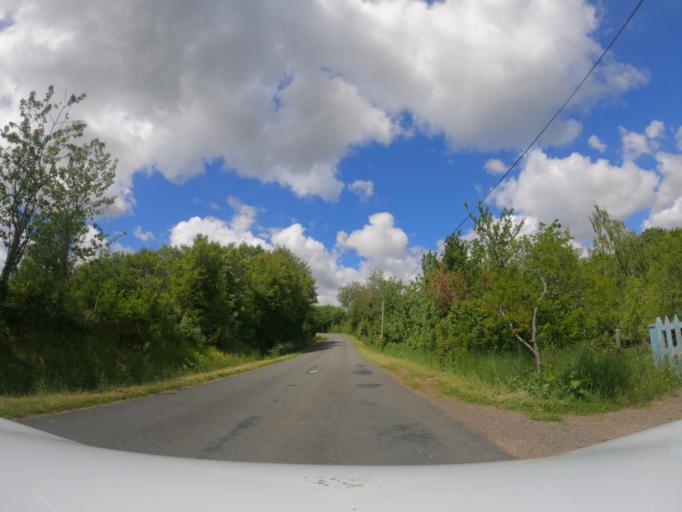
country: FR
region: Pays de la Loire
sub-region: Departement de la Vendee
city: Le Champ-Saint-Pere
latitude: 46.5055
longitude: -1.3554
